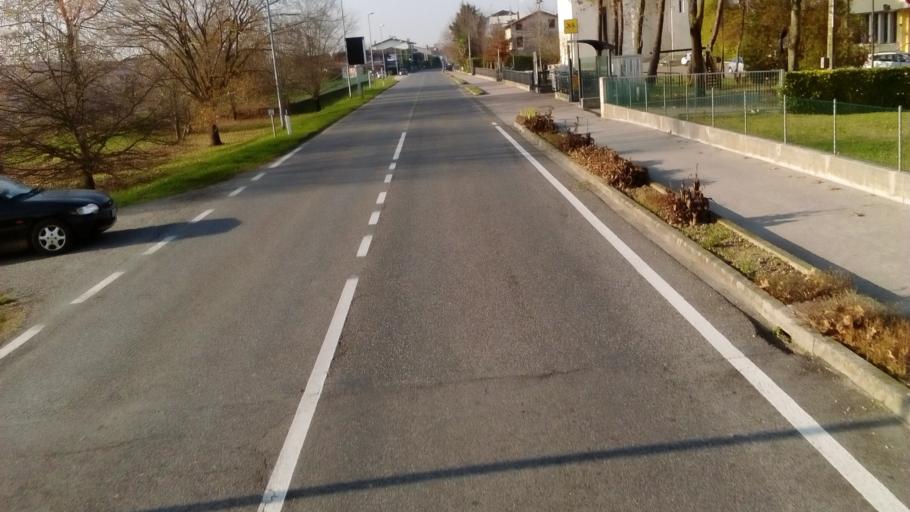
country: IT
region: Friuli Venezia Giulia
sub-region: Provincia di Udine
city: San Giorgio di Nogaro
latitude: 45.8330
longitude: 13.1828
